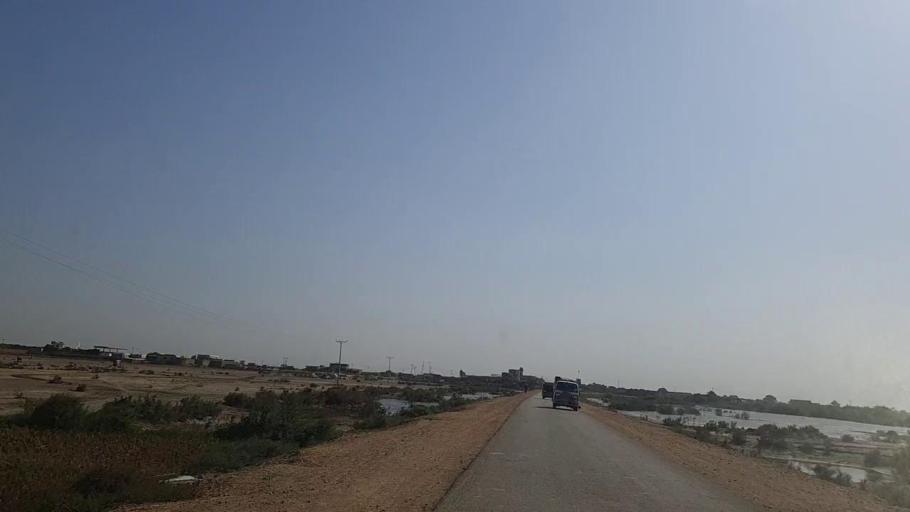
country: PK
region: Sindh
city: Mirpur Batoro
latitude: 24.6228
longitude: 68.2948
